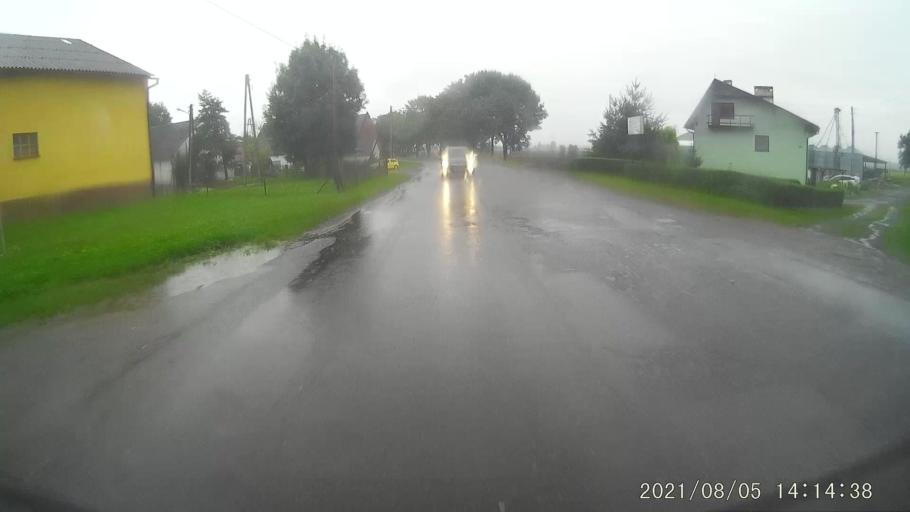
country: PL
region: Opole Voivodeship
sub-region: Powiat prudnicki
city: Biala
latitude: 50.4671
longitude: 17.7388
